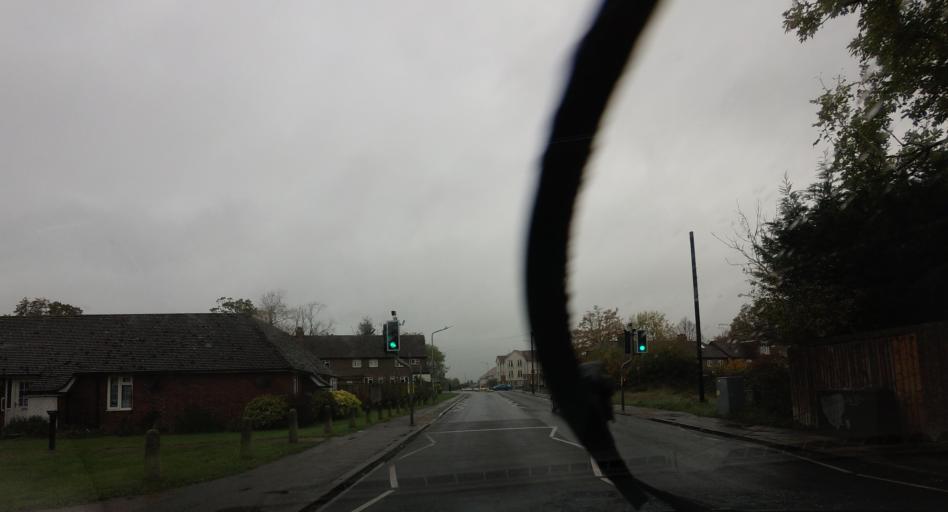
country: GB
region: England
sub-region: Kent
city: Tonbridge
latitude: 51.2094
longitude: 0.2800
